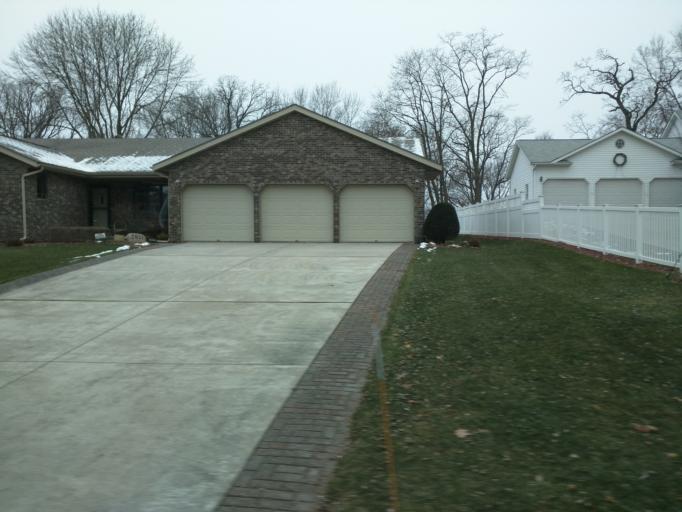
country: US
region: Wisconsin
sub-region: La Crosse County
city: French Island
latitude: 43.8665
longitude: -91.2732
